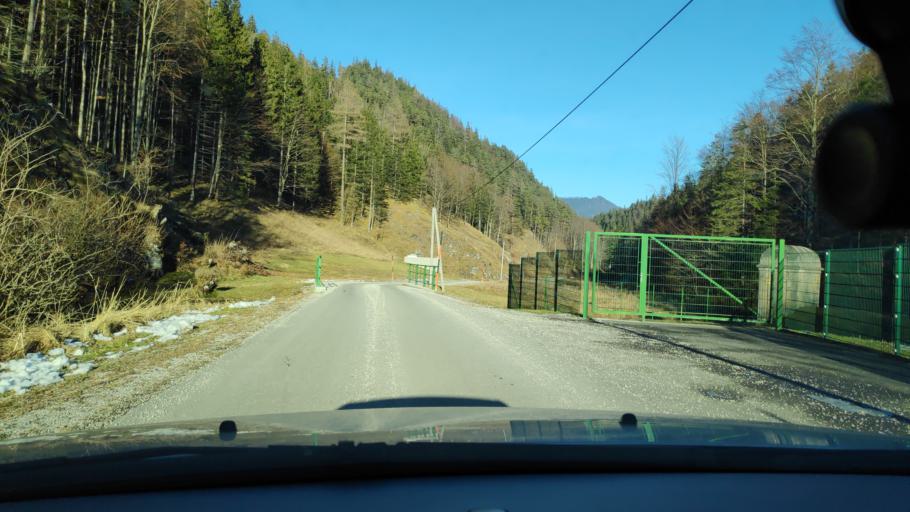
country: AT
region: Lower Austria
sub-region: Politischer Bezirk Neunkirchen
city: Schwarzau im Gebirge
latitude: 47.7442
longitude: 15.6729
